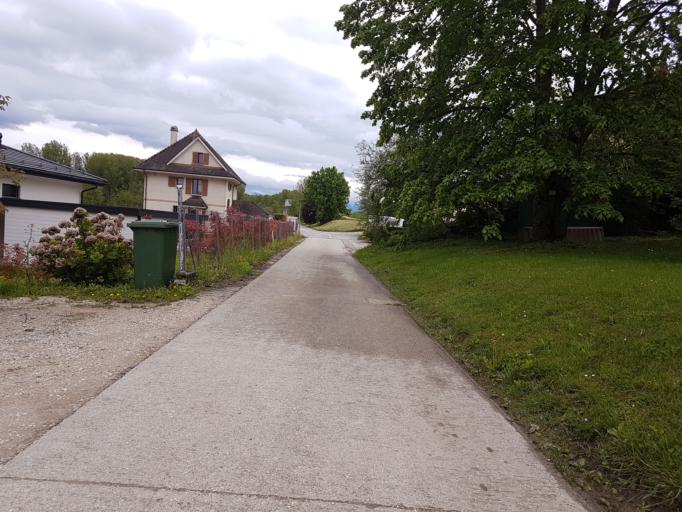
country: CH
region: Vaud
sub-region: Morges District
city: Preverenges
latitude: 46.5243
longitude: 6.5432
